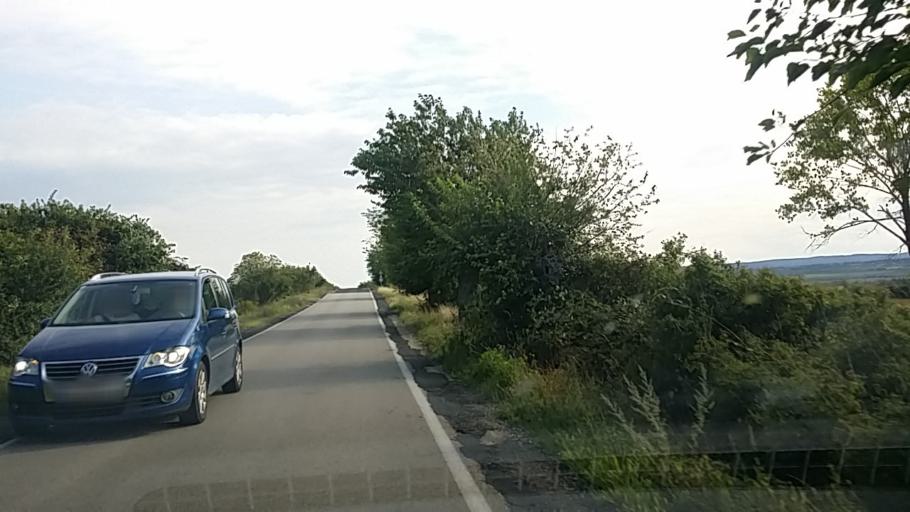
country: HU
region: Gyor-Moson-Sopron
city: Fertorakos
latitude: 47.7476
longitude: 16.6214
